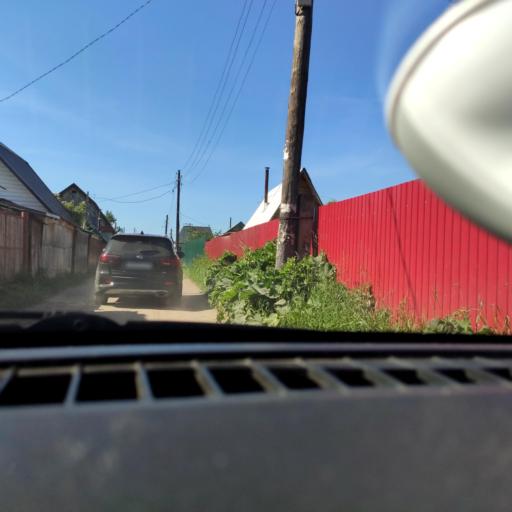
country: RU
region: Perm
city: Overyata
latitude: 58.0059
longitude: 55.8707
